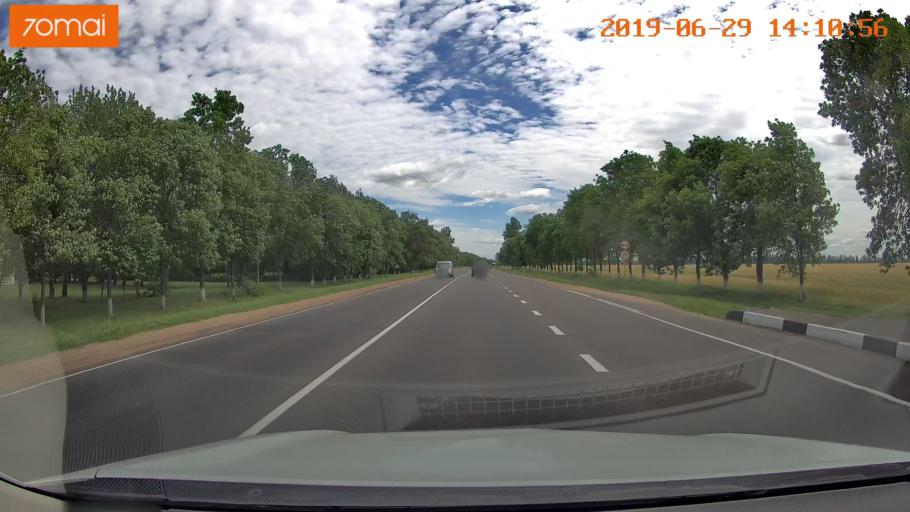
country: BY
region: Minsk
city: Salihorsk
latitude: 52.8247
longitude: 27.4988
